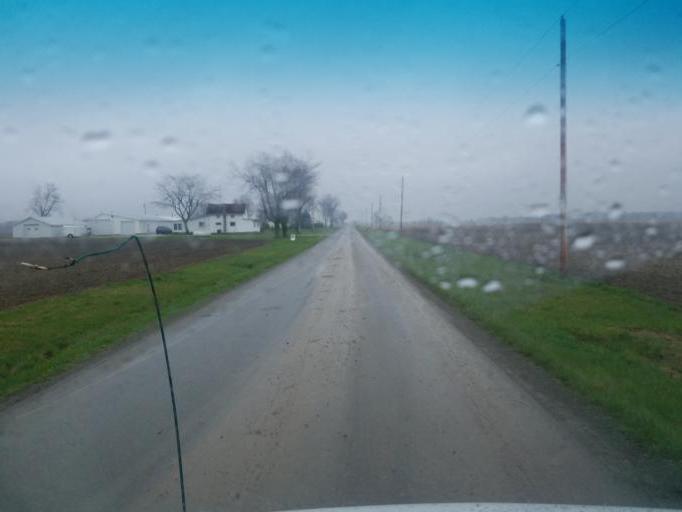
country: US
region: Ohio
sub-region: Wyandot County
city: Carey
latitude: 40.9854
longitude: -83.2903
